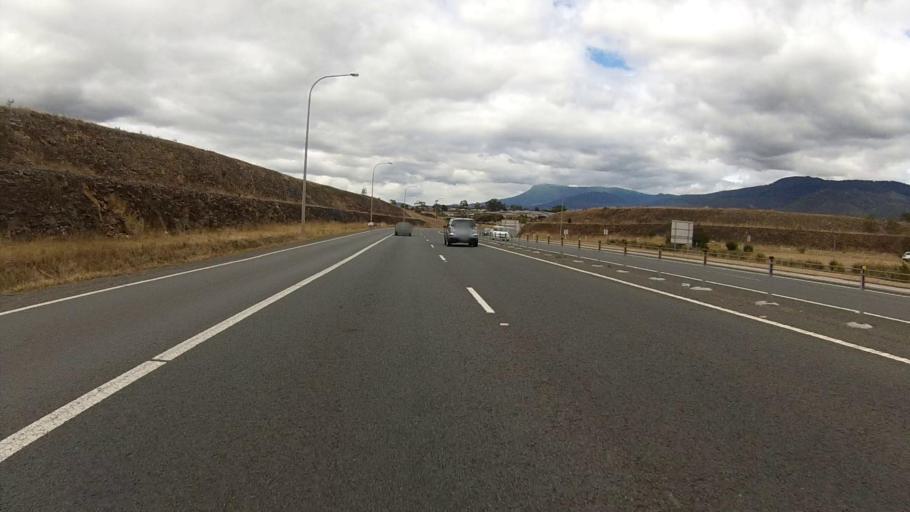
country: AU
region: Tasmania
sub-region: Brighton
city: Bridgewater
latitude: -42.7284
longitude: 147.2374
